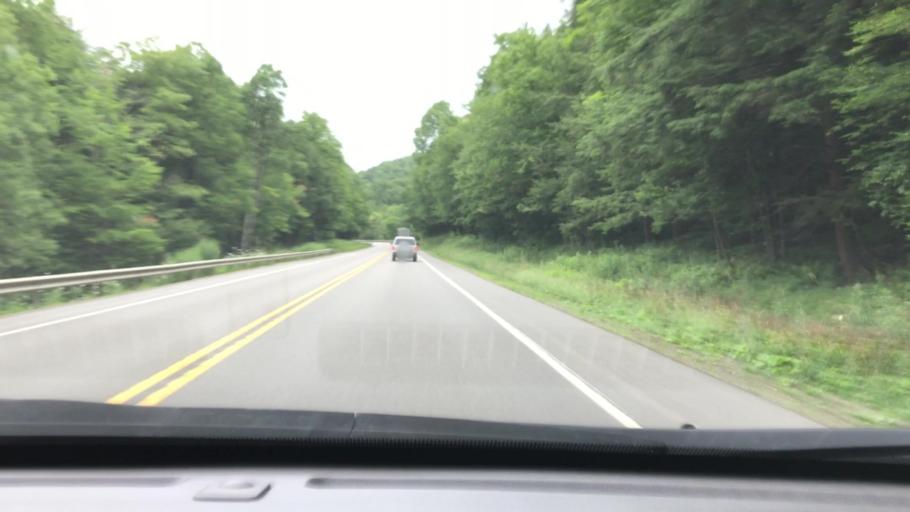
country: US
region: Pennsylvania
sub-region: McKean County
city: Kane
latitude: 41.6669
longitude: -78.6811
